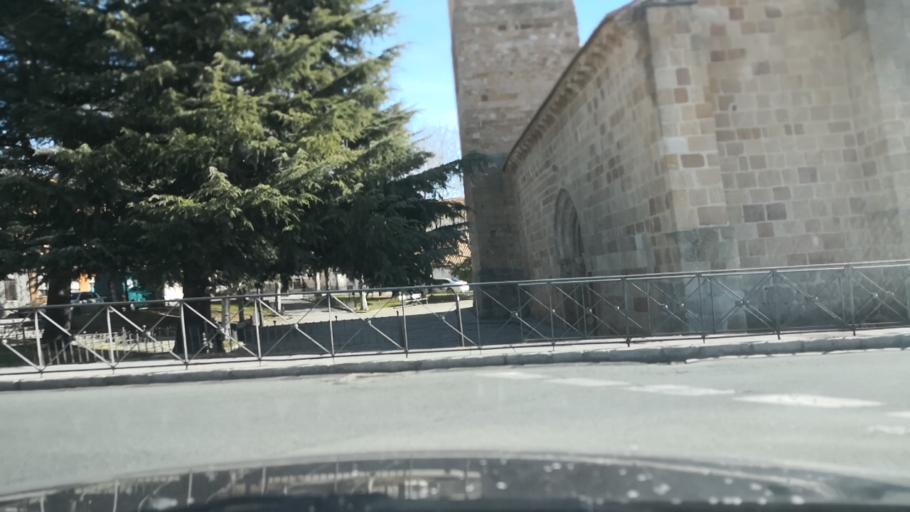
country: ES
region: Castille and Leon
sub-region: Provincia de Avila
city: Avila
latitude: 40.6520
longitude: -4.7027
